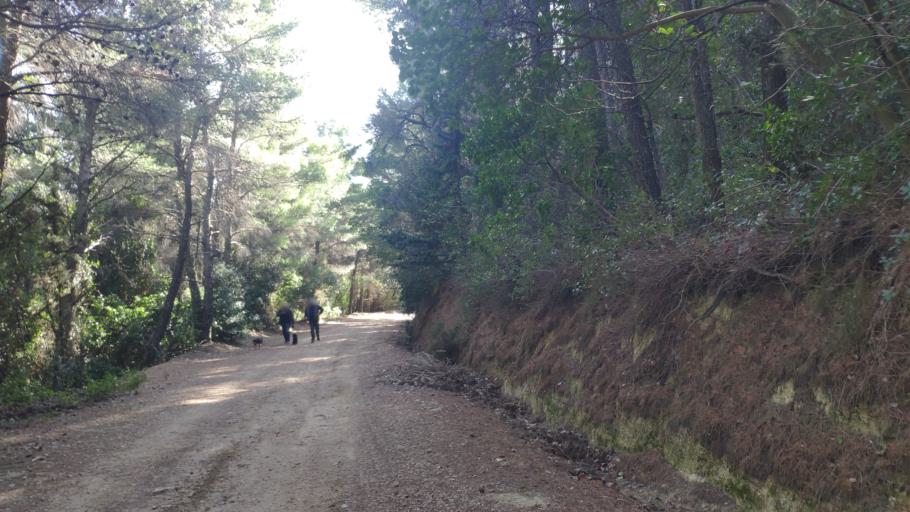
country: GR
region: Attica
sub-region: Nomarchia Anatolikis Attikis
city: Varybobi
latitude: 38.1582
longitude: 23.7761
